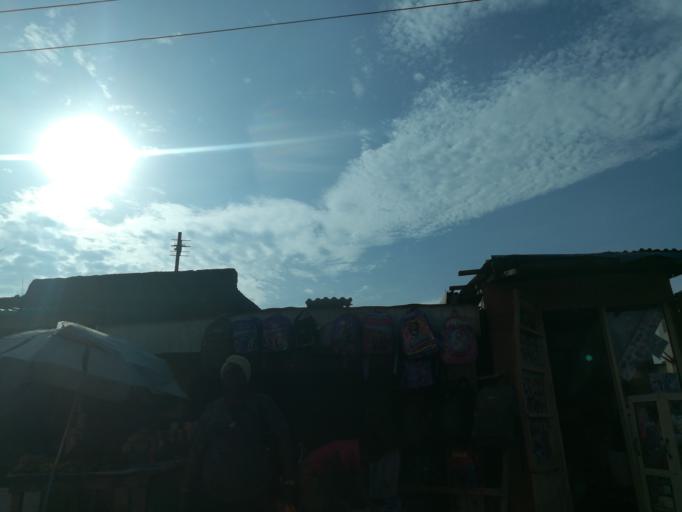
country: NG
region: Lagos
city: Ojota
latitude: 6.6036
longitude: 3.4193
